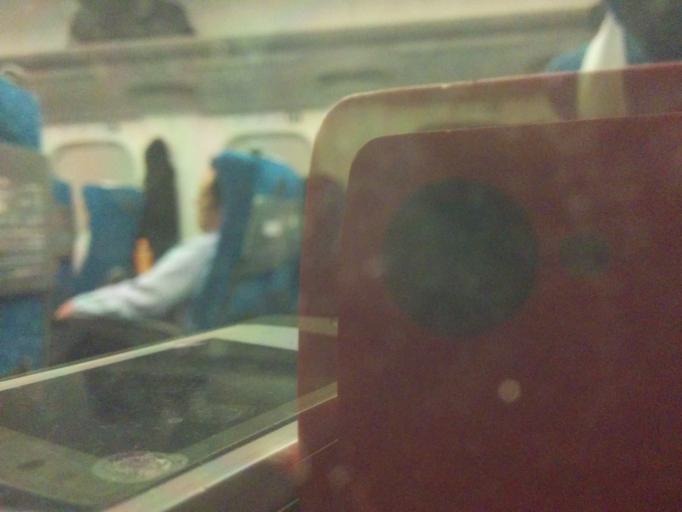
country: JP
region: Shizuoka
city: Fukuroi
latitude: 34.7411
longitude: 137.9327
